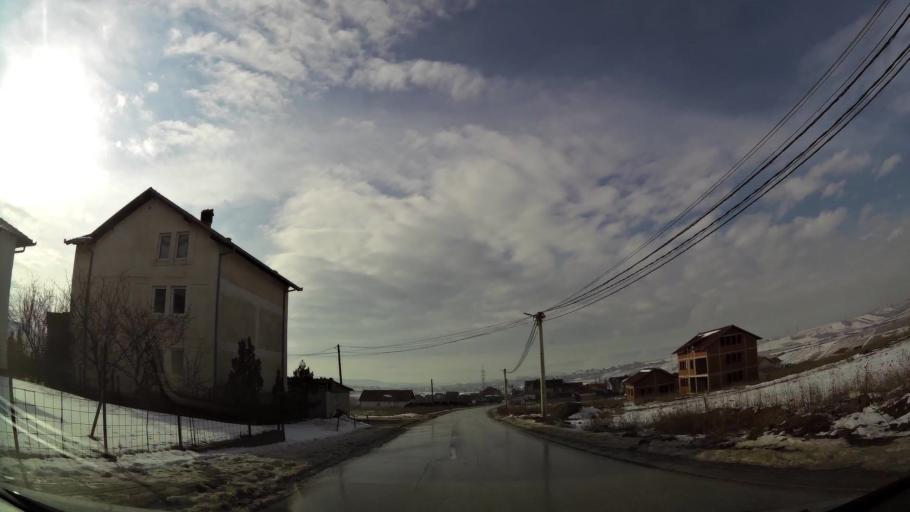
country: XK
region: Pristina
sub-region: Komuna e Prishtines
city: Pristina
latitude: 42.6728
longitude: 21.1442
